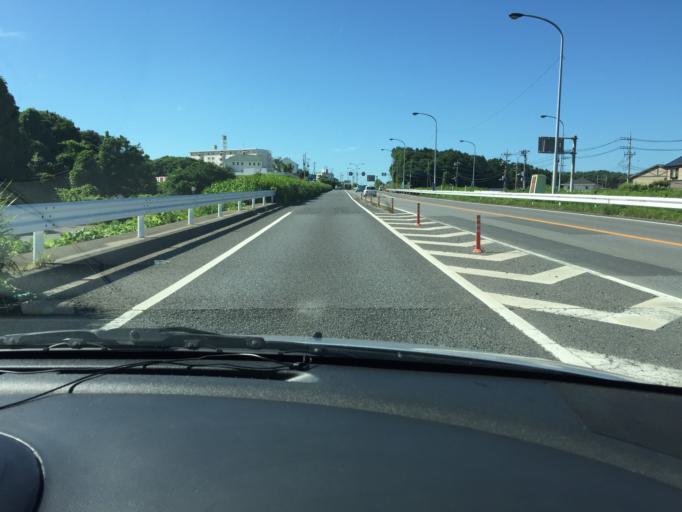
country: JP
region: Ibaraki
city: Naka
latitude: 36.0751
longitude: 140.1787
